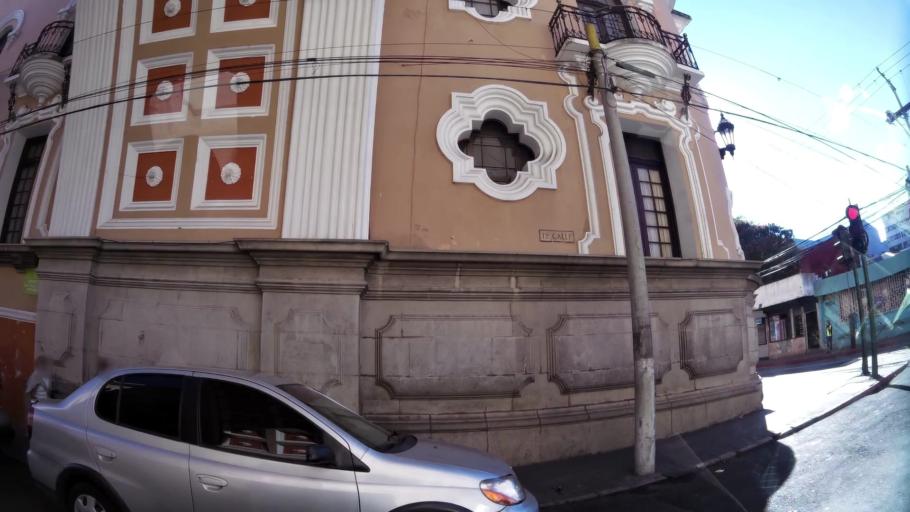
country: GT
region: Guatemala
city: Guatemala City
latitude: 14.6371
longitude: -90.5130
